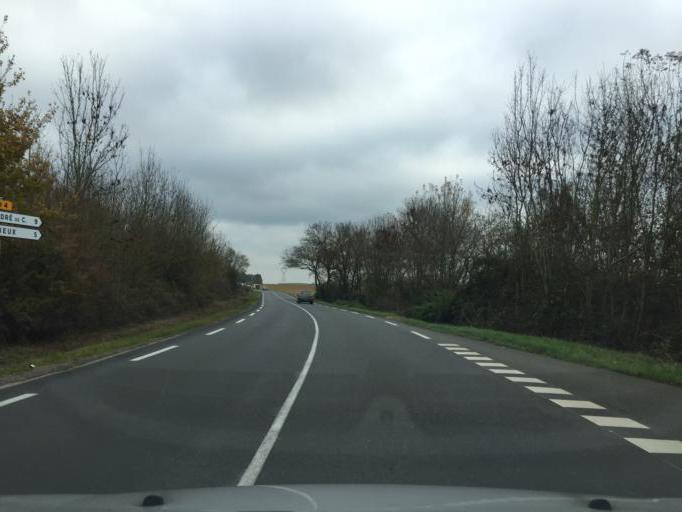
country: FR
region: Rhone-Alpes
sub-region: Departement de l'Ain
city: Reyrieux
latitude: 45.9386
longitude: 4.8360
